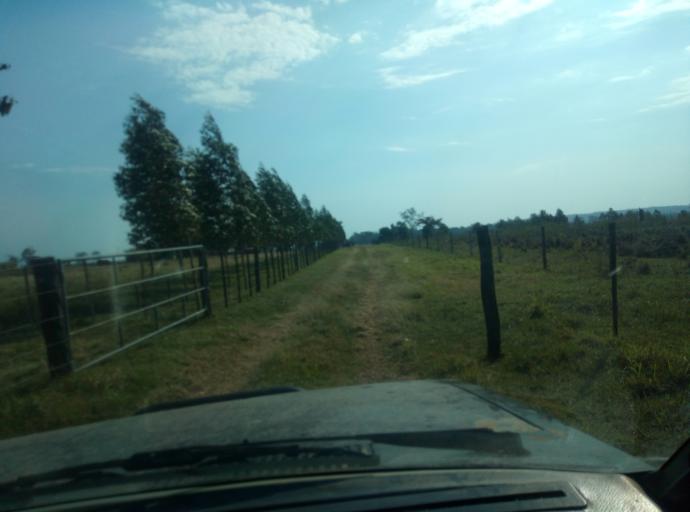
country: PY
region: Caaguazu
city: Doctor Cecilio Baez
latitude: -25.1412
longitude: -56.2604
